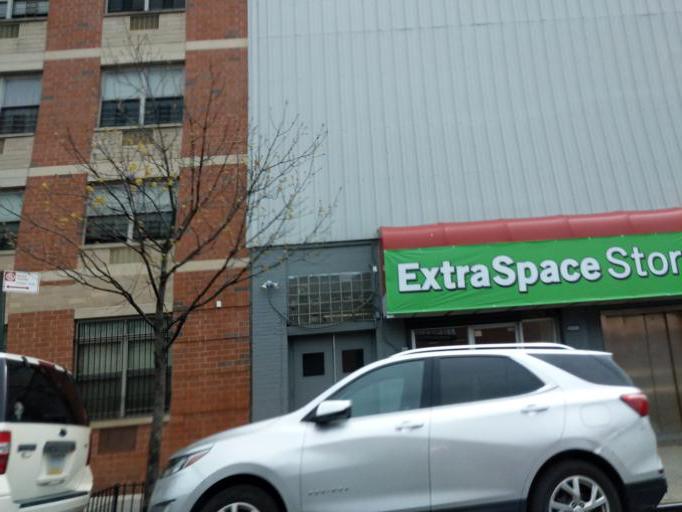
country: US
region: New York
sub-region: Bronx
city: The Bronx
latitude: 40.8482
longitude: -73.8954
